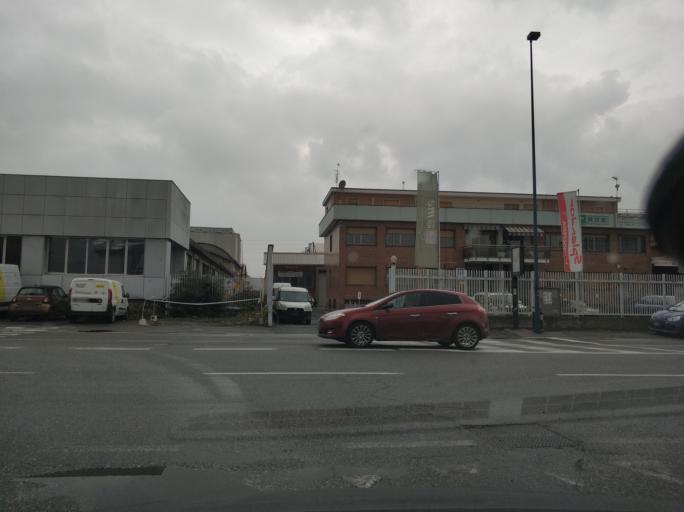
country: IT
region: Piedmont
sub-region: Provincia di Torino
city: Settimo Torinese
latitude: 45.1226
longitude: 7.7452
